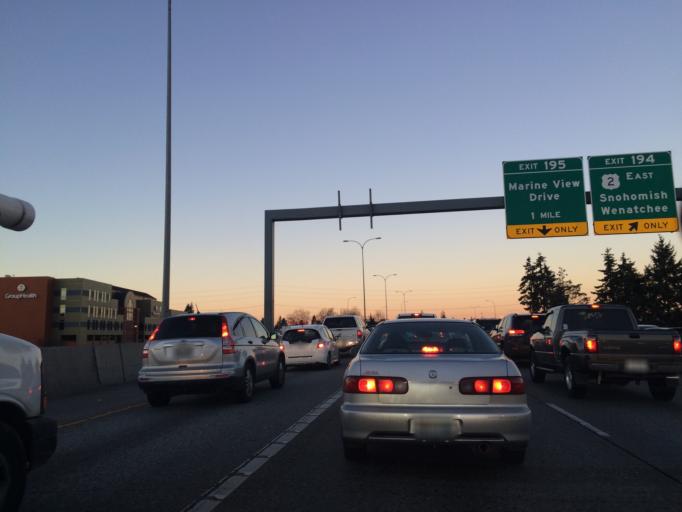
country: US
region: Washington
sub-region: Snohomish County
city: Everett
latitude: 47.9761
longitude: -122.1906
